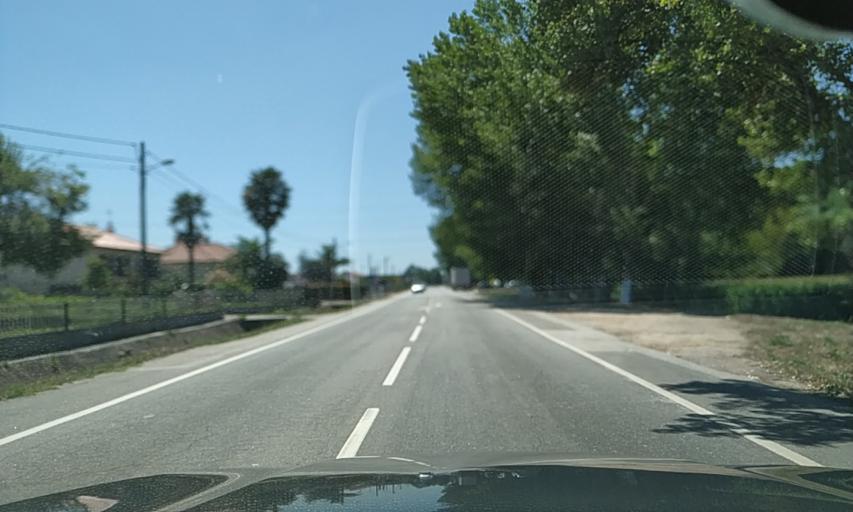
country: PT
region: Aveiro
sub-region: Anadia
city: Sangalhos
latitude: 40.4731
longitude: -8.4542
